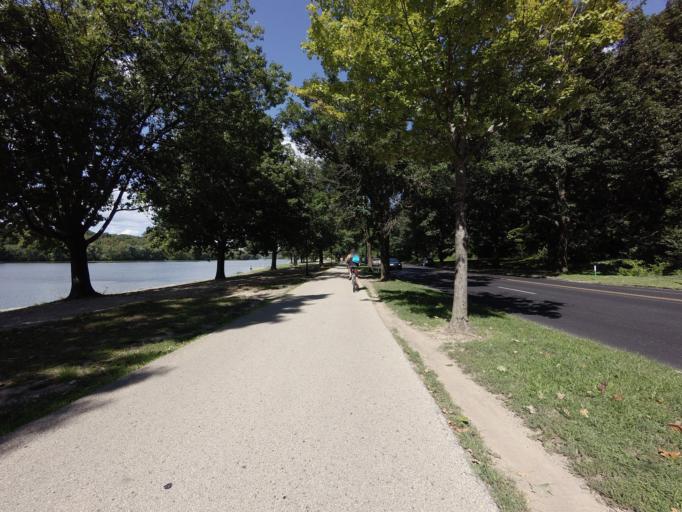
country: US
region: Pennsylvania
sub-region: Montgomery County
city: Bala-Cynwyd
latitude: 39.9888
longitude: -75.1987
